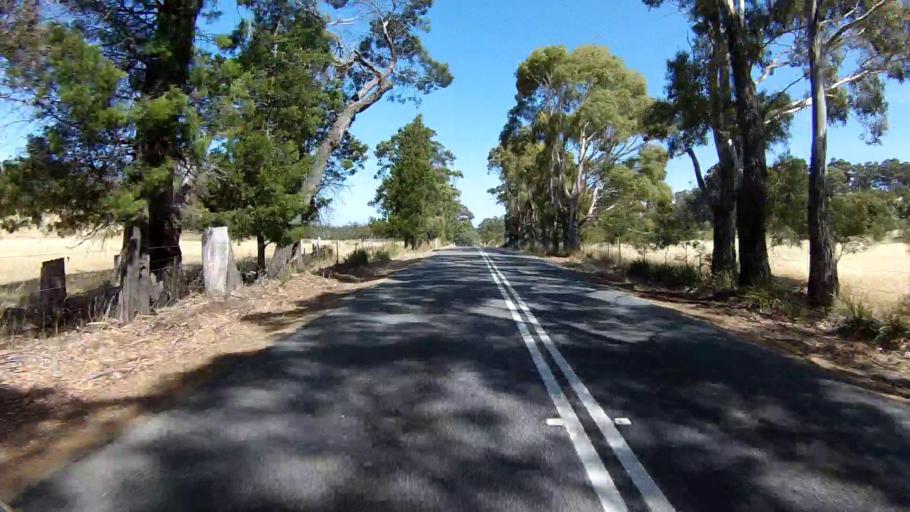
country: AU
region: Tasmania
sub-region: Sorell
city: Sorell
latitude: -42.3101
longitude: 147.9619
